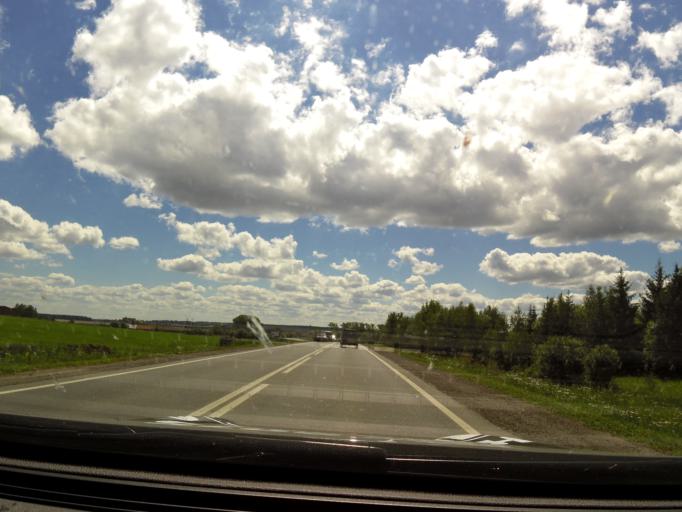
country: RU
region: Vologda
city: Molochnoye
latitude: 59.2941
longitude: 39.6885
